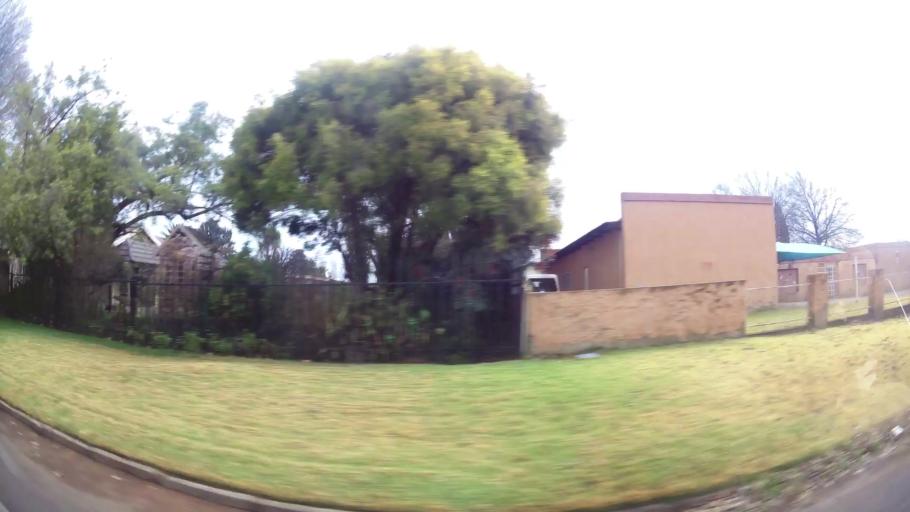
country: ZA
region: Gauteng
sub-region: Sedibeng District Municipality
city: Meyerton
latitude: -26.6018
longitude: 27.9976
